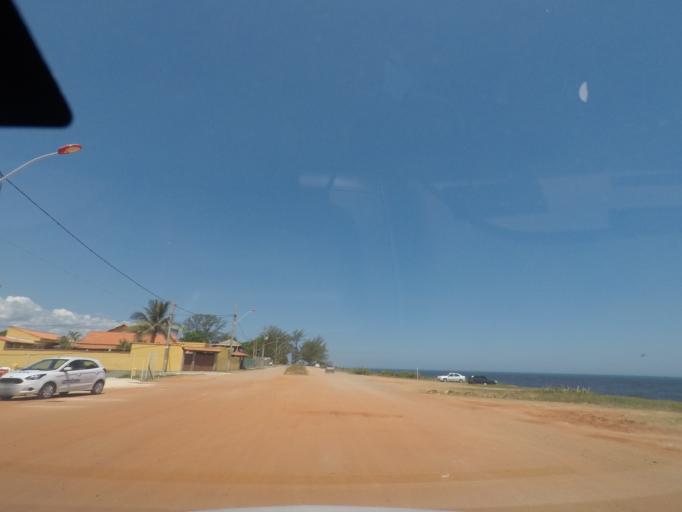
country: BR
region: Rio de Janeiro
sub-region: Marica
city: Marica
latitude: -22.9736
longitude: -42.9302
